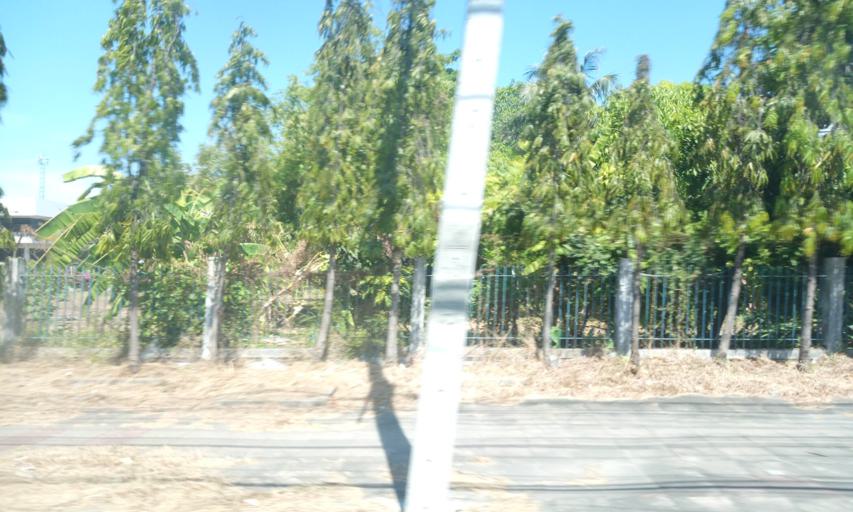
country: TH
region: Samut Prakan
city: Bang Bo District
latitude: 13.5783
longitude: 100.7954
